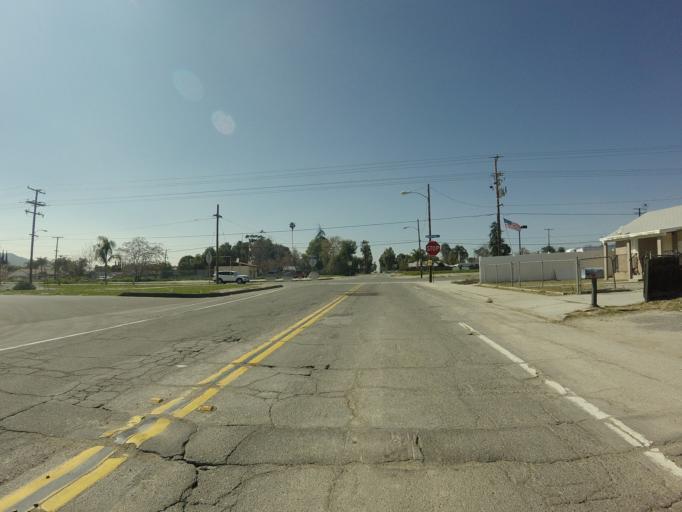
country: US
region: California
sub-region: Riverside County
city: Moreno Valley
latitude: 33.9175
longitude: -117.1562
